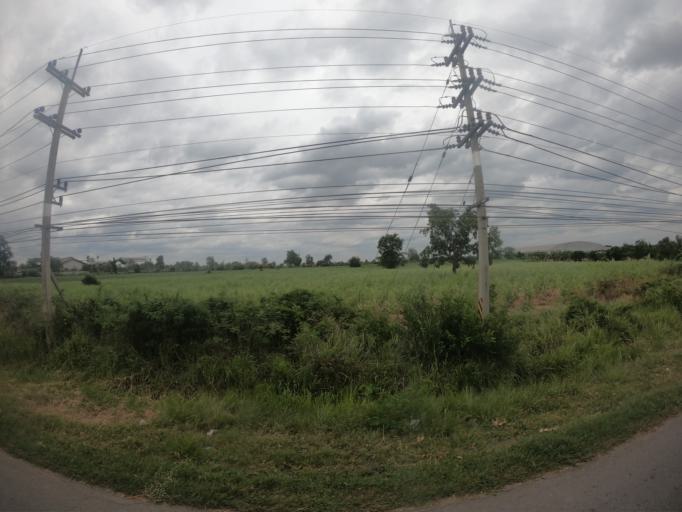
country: TH
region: Nakhon Ratchasima
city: Chok Chai
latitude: 14.7757
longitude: 102.1620
